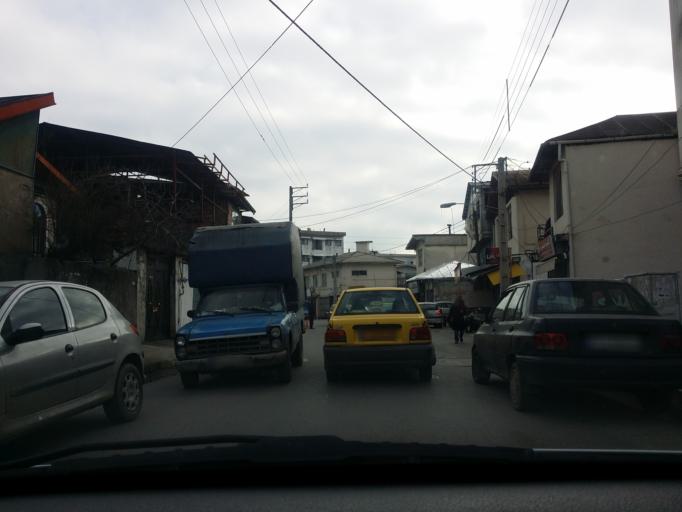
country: IR
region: Mazandaran
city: Chalus
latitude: 36.6569
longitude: 51.4135
